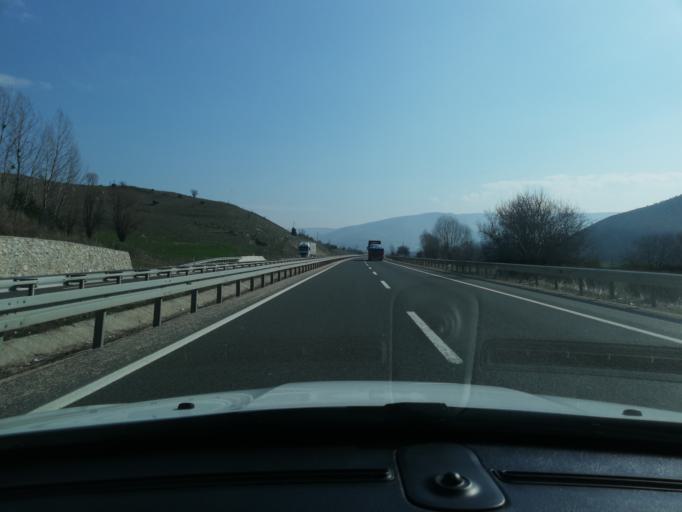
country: TR
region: Cankiri
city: Cerkes
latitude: 40.8346
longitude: 32.7405
